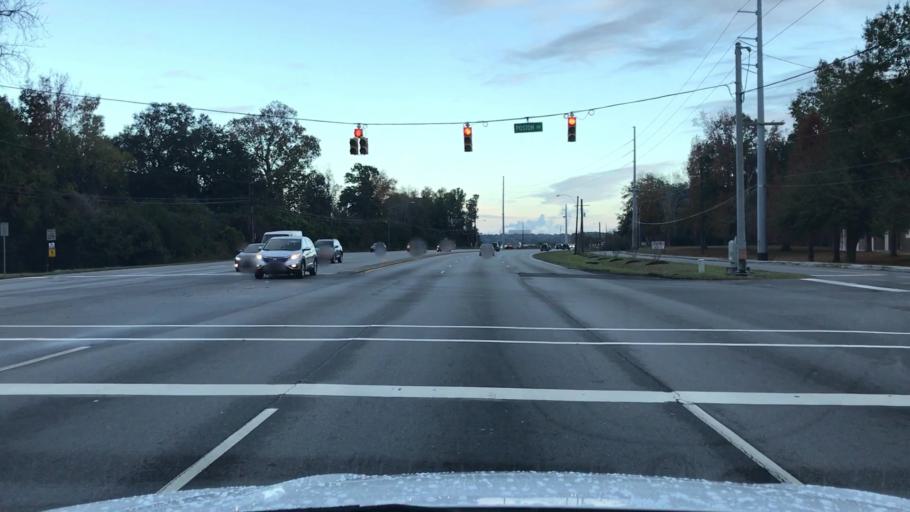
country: US
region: South Carolina
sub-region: Charleston County
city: North Charleston
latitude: 32.8271
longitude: -79.9902
